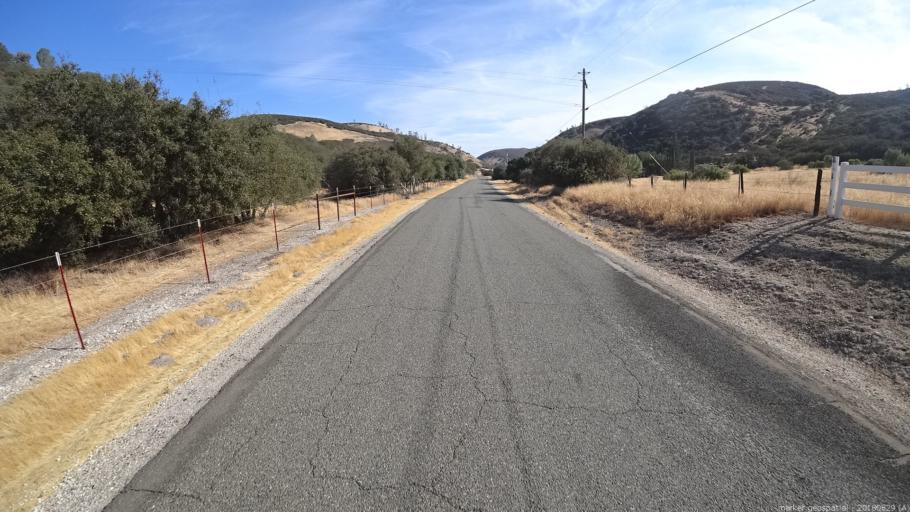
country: US
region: California
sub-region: Monterey County
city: King City
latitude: 35.9873
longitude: -121.0778
